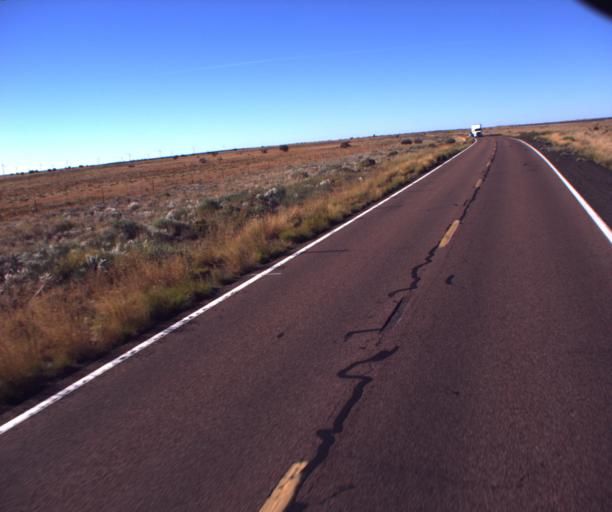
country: US
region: Arizona
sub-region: Navajo County
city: Holbrook
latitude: 34.7229
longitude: -110.2922
